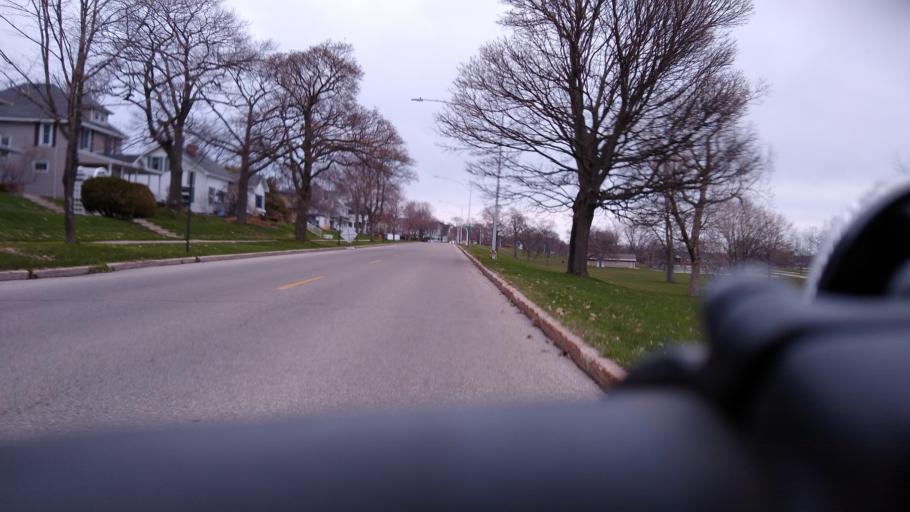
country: US
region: Michigan
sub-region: Delta County
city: Escanaba
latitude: 45.7377
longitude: -87.0578
